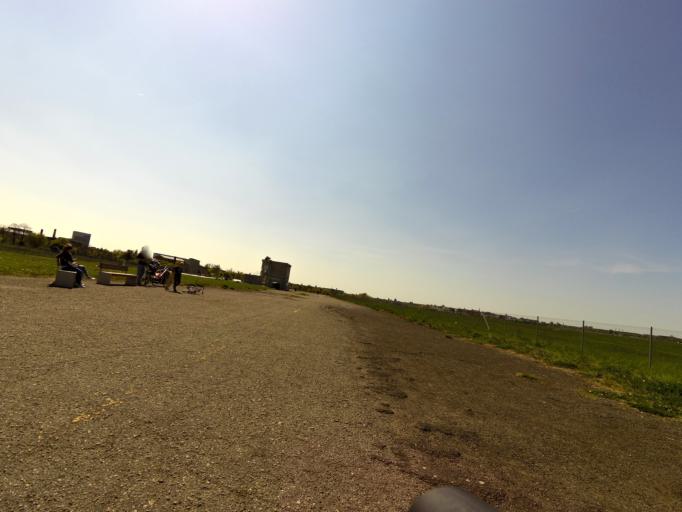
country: DE
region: Berlin
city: Tempelhof Bezirk
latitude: 52.4691
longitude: 13.4135
